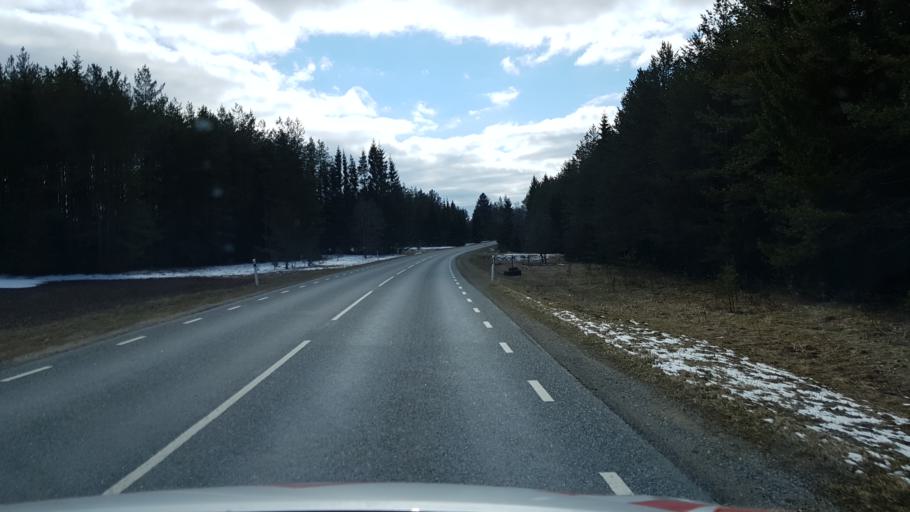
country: EE
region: Laeaene-Virumaa
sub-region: Tapa vald
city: Tapa
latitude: 59.2878
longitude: 25.9971
